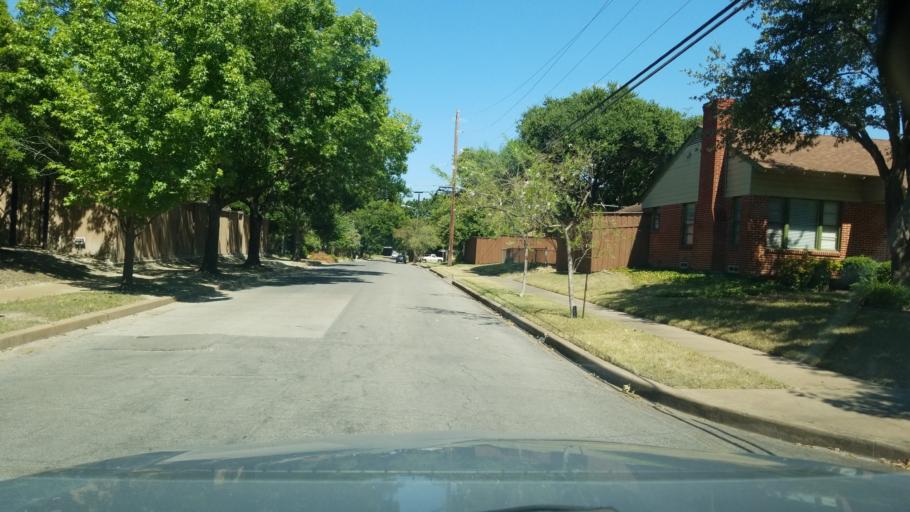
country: US
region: Texas
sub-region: Dallas County
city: Cockrell Hill
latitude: 32.7292
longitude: -96.8556
